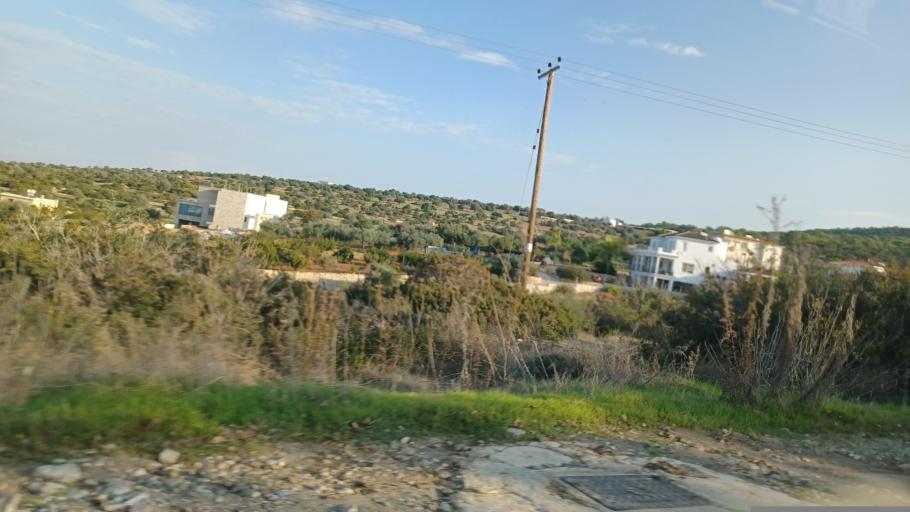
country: CY
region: Pafos
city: Pegeia
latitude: 34.8945
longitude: 32.3414
